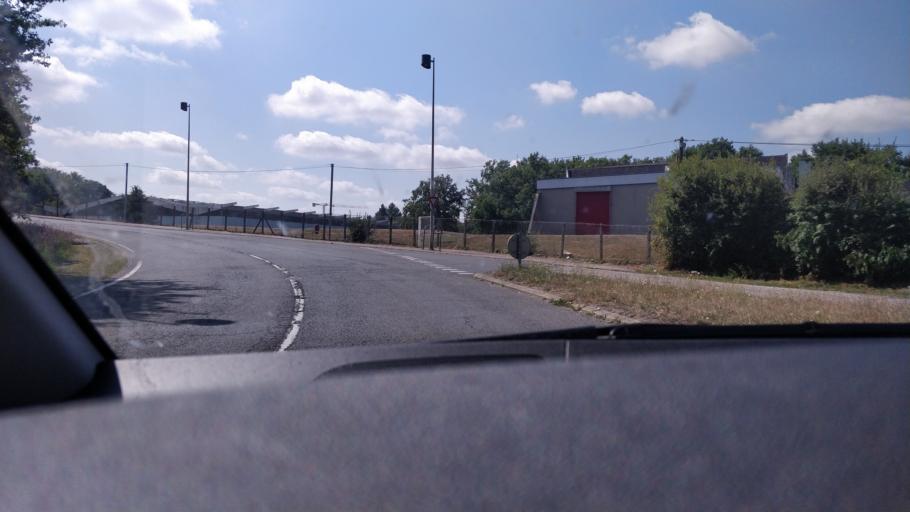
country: FR
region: Limousin
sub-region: Departement de la Haute-Vienne
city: Limoges
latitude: 45.8620
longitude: 1.2707
